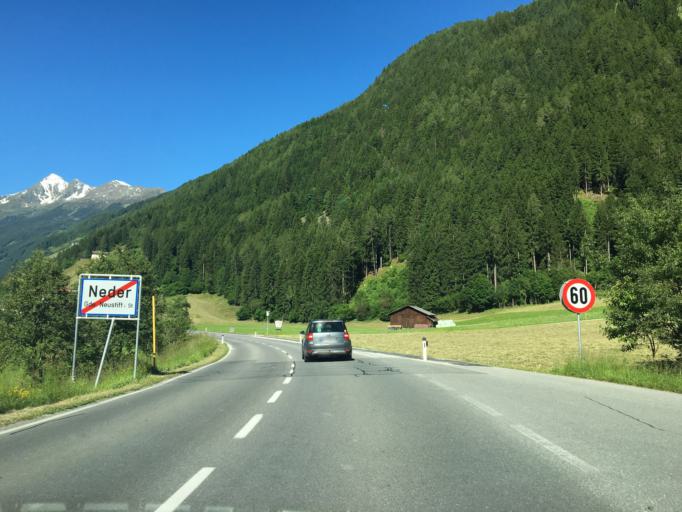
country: AT
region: Tyrol
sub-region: Politischer Bezirk Innsbruck Land
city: Neustift im Stubaital
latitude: 47.1220
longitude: 11.3248
